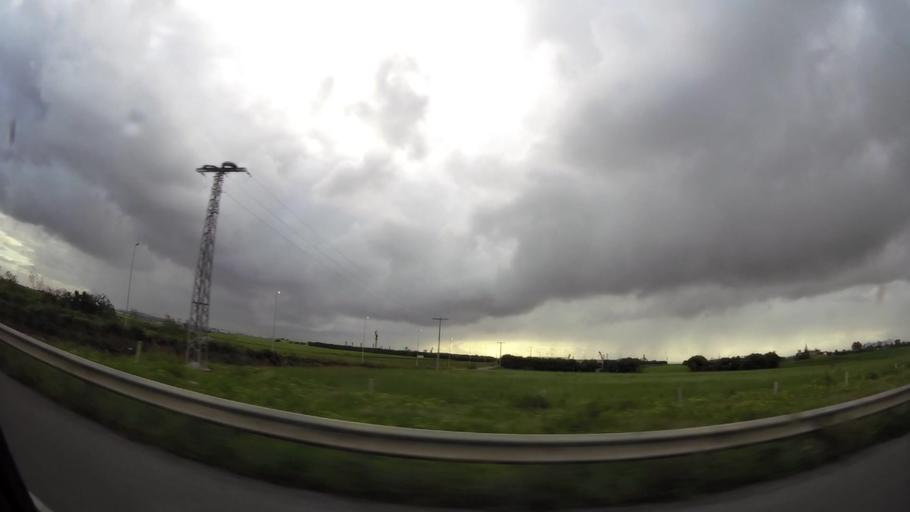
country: MA
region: Grand Casablanca
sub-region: Mediouna
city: Tit Mellil
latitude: 33.6141
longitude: -7.4340
